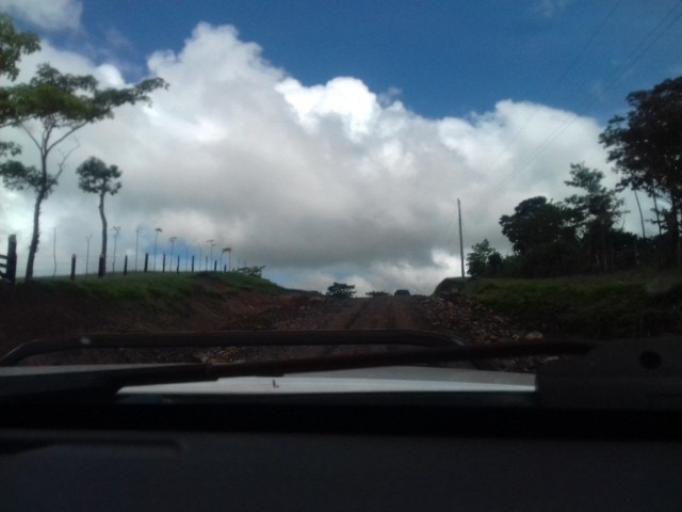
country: NI
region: Matagalpa
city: Rio Blanco
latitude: 12.9798
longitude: -85.1854
